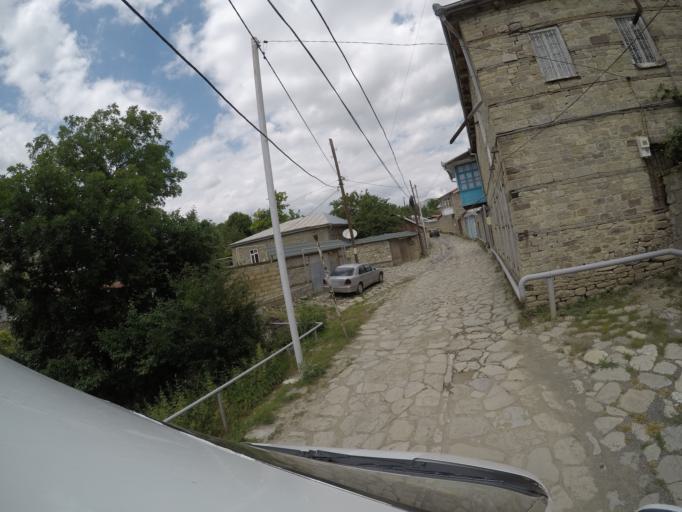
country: AZ
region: Ismayilli
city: Basqal
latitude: 40.8495
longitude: 48.3885
